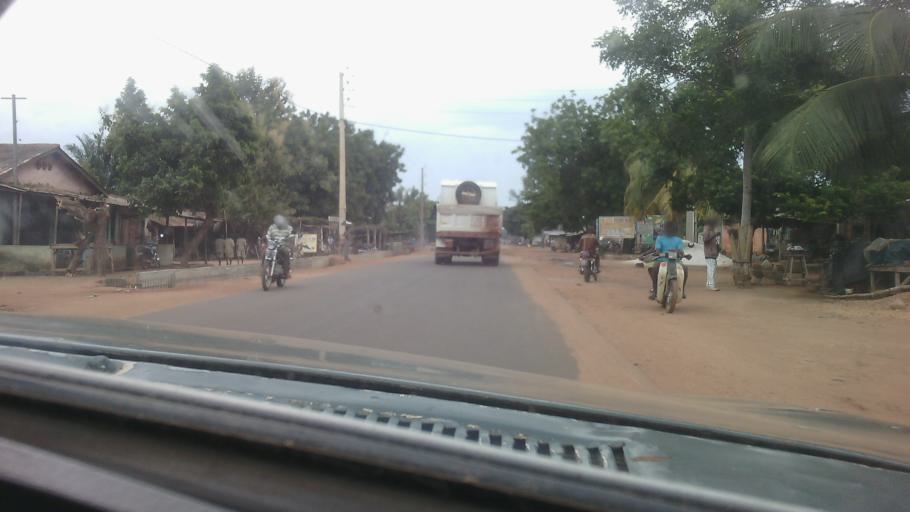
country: BJ
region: Mono
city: Come
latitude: 6.5163
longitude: 1.8232
